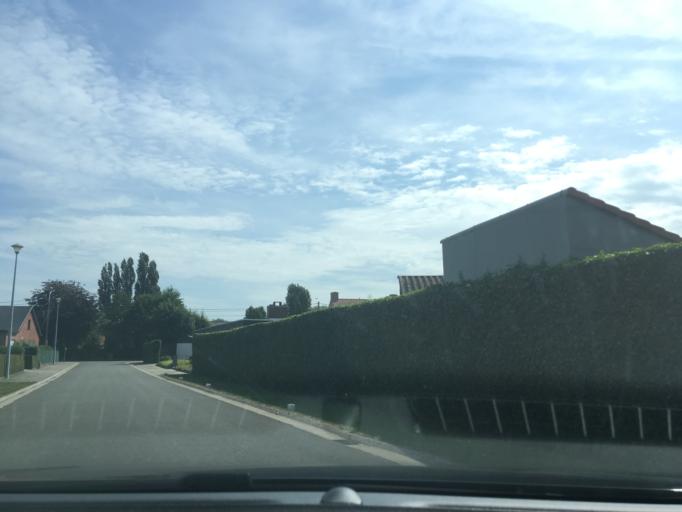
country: BE
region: Flanders
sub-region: Provincie West-Vlaanderen
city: Ledegem
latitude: 50.8946
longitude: 3.1211
